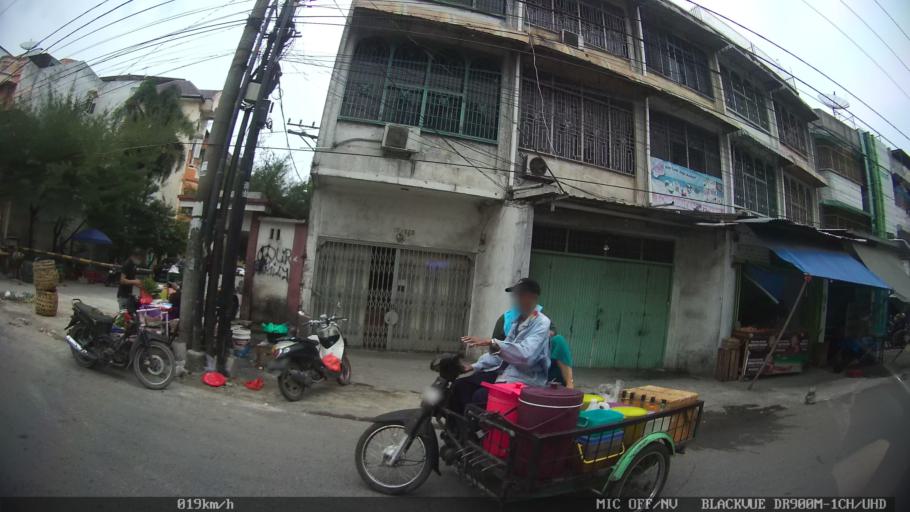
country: ID
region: North Sumatra
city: Medan
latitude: 3.5839
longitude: 98.7043
